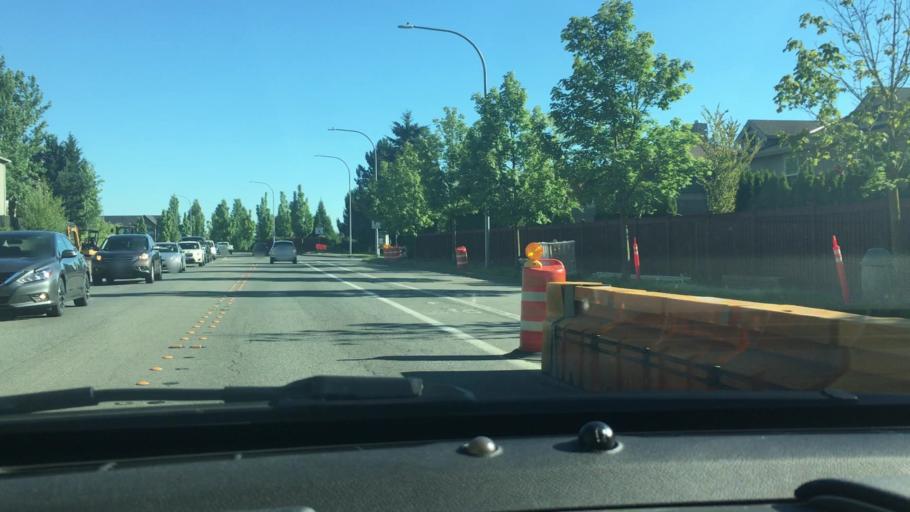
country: US
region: Washington
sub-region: King County
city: Redmond
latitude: 47.6964
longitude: -122.1322
